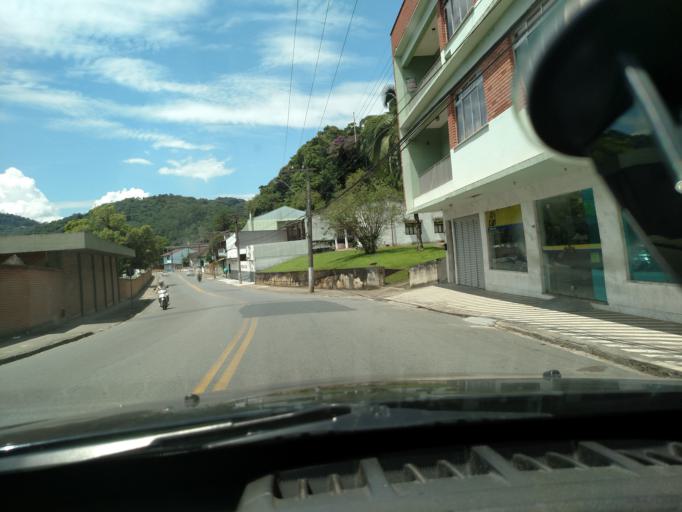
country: BR
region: Santa Catarina
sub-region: Blumenau
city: Blumenau
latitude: -26.9634
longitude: -49.0724
